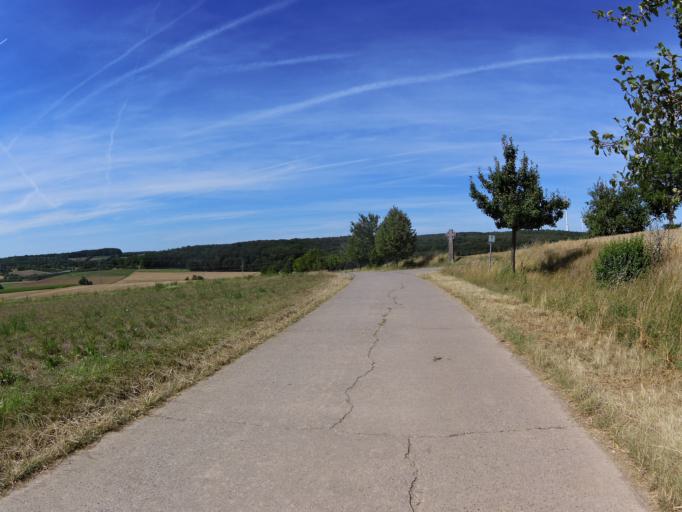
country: DE
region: Bavaria
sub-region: Regierungsbezirk Unterfranken
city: Hettstadt
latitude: 49.8093
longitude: 9.8130
